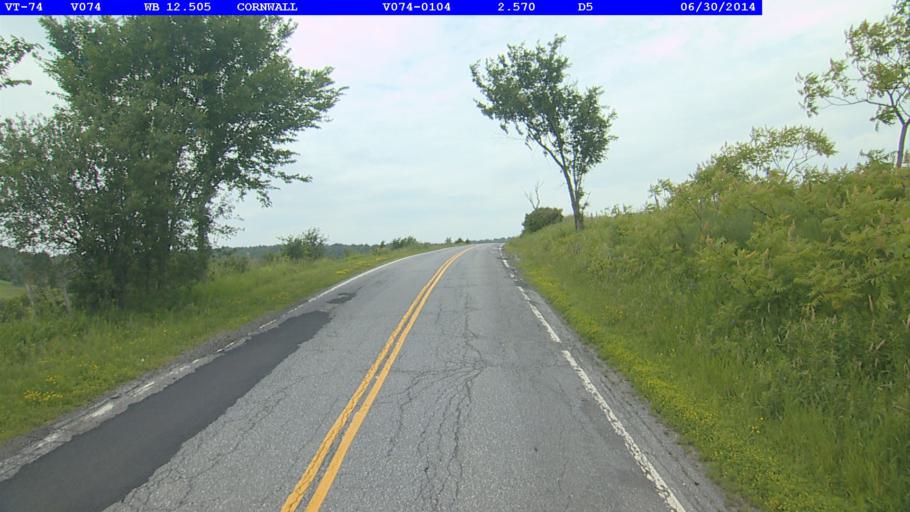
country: US
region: Vermont
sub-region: Addison County
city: Middlebury (village)
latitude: 43.9575
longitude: -73.2147
